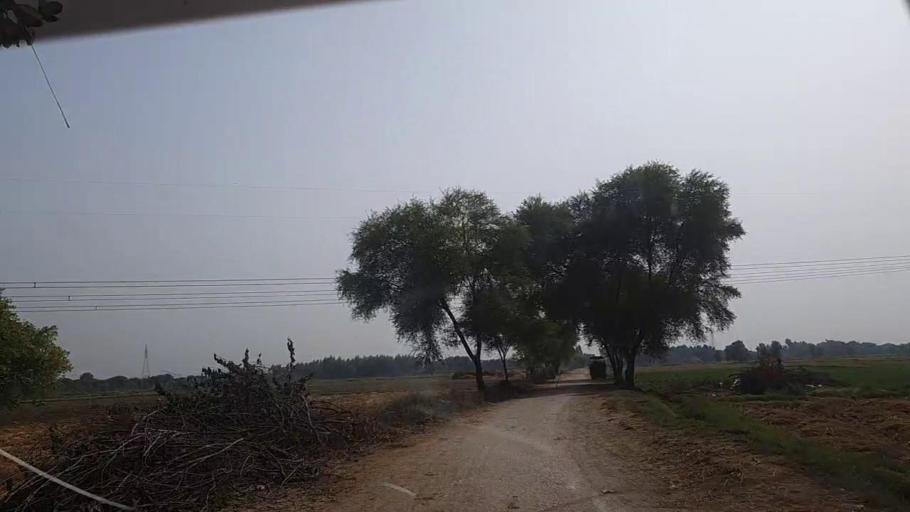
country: PK
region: Sindh
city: Madeji
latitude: 27.7388
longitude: 68.4357
